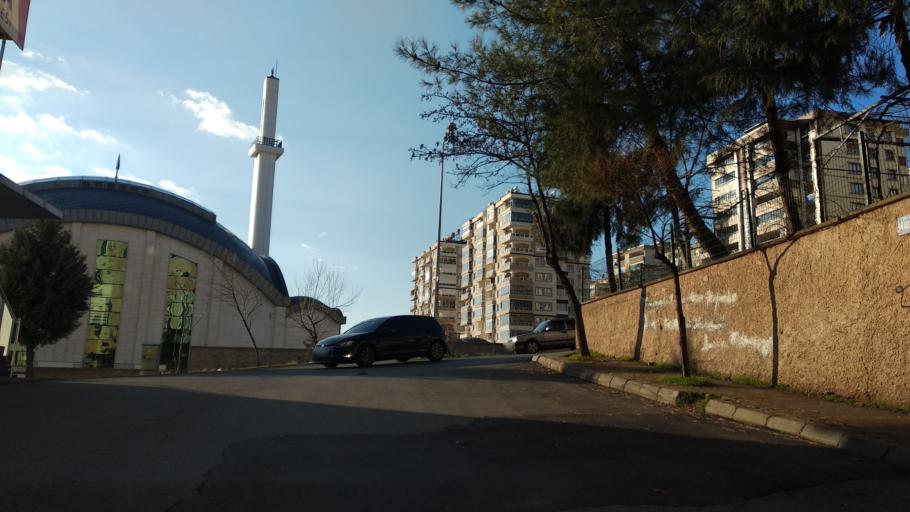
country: TR
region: Kahramanmaras
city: Kahramanmaras
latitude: 37.5895
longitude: 36.8831
